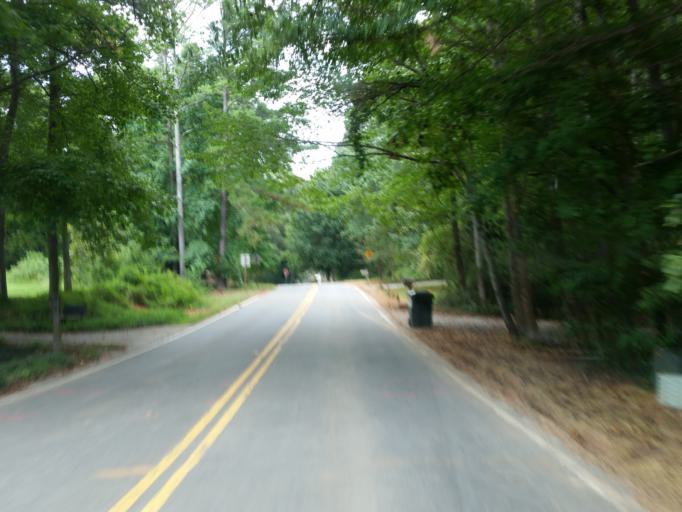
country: US
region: Georgia
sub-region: Fulton County
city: Sandy Springs
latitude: 33.9531
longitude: -84.4543
